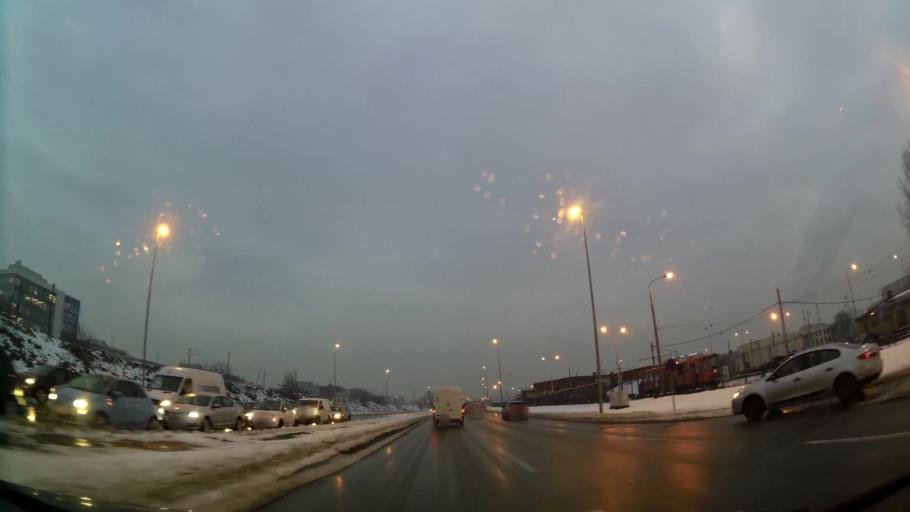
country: RS
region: Central Serbia
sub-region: Belgrade
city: Novi Beograd
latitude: 44.8110
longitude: 20.4074
